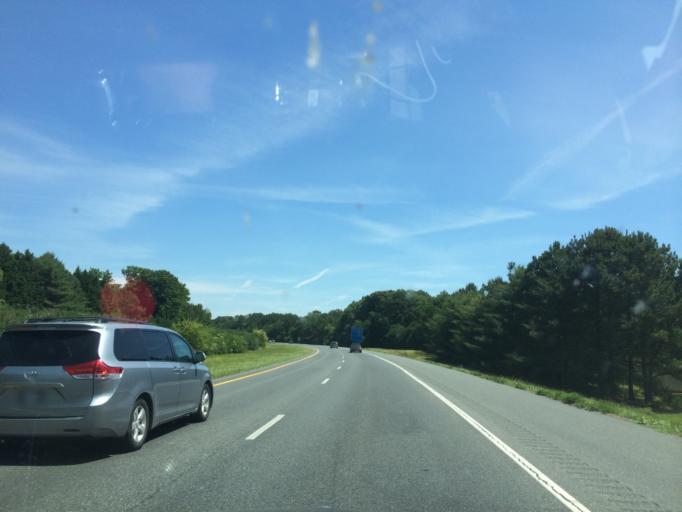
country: US
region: Maryland
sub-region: Wicomico County
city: Salisbury
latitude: 38.3432
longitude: -75.5462
